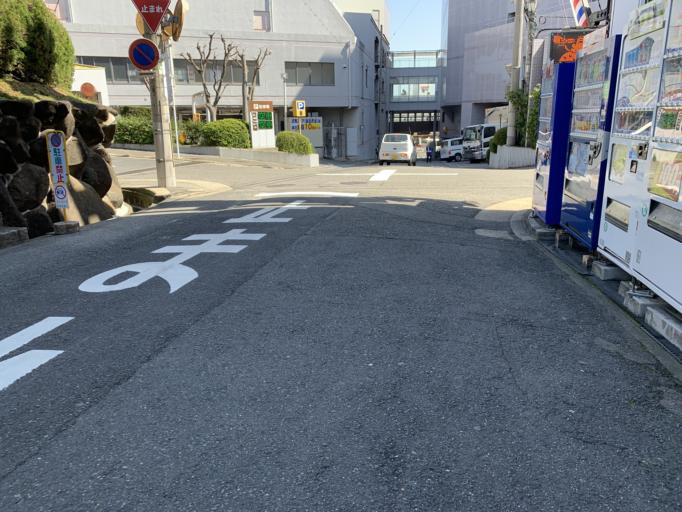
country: JP
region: Nara
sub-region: Ikoma-shi
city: Ikoma
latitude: 34.6986
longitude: 135.7501
